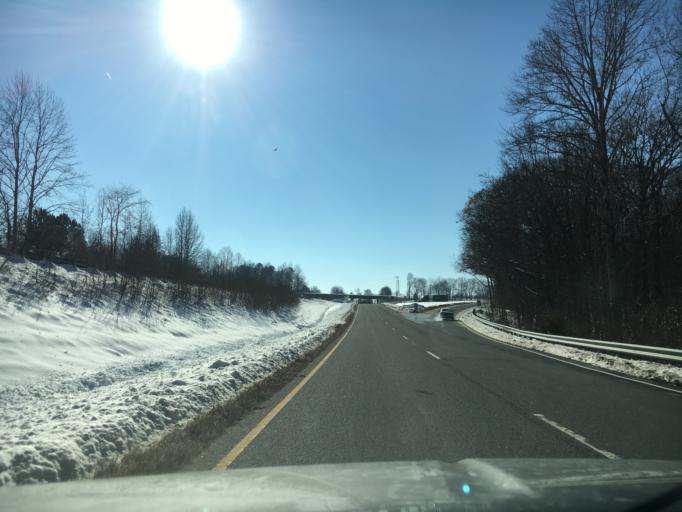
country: US
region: Virginia
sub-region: Nottoway County
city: Crewe
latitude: 37.2765
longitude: -78.1174
